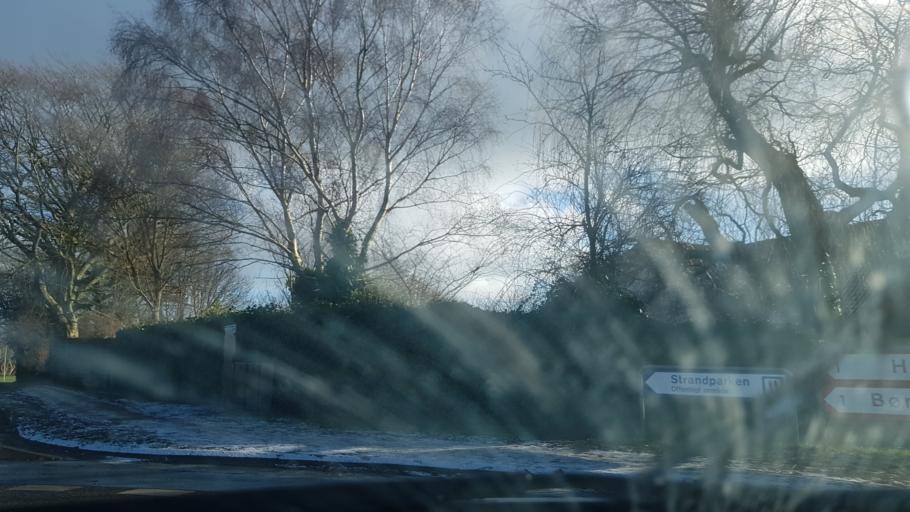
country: DK
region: South Denmark
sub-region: Fredericia Kommune
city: Taulov
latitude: 55.5189
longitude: 9.6347
